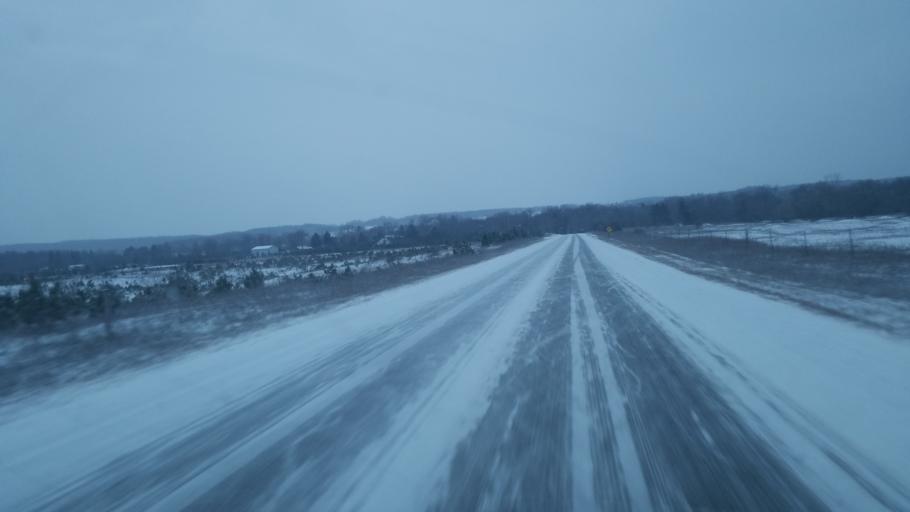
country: US
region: Michigan
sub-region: Osceola County
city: Reed City
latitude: 43.8485
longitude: -85.4262
